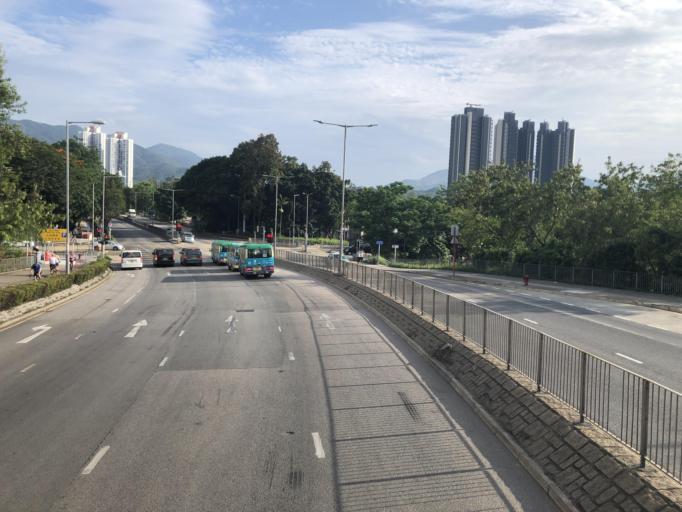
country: CN
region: Guangdong
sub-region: Shenzhen
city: Shenzhen
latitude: 22.5041
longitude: 114.1237
